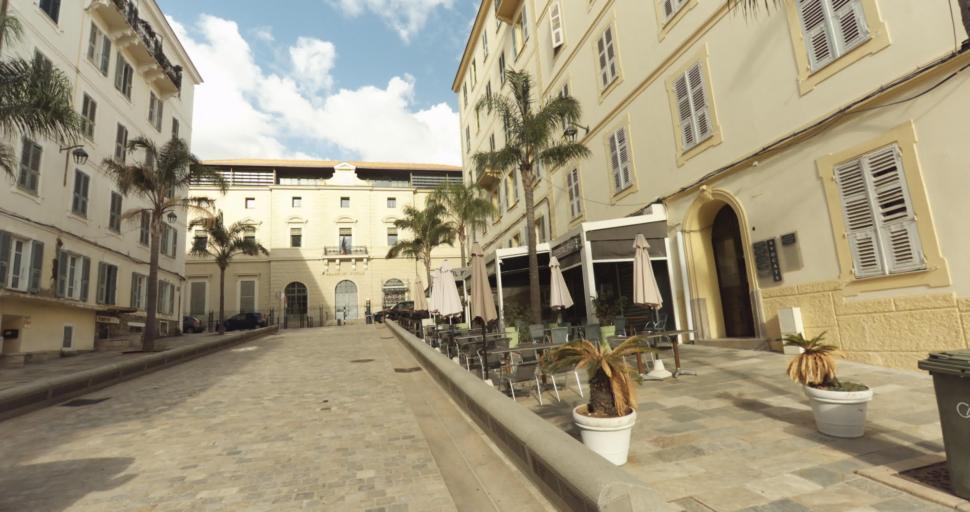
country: FR
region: Corsica
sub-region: Departement de la Corse-du-Sud
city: Ajaccio
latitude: 41.9256
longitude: 8.7375
